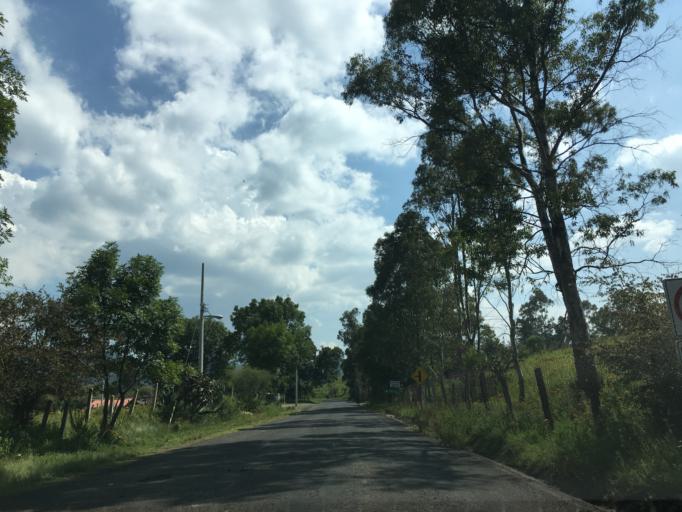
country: MX
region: Michoacan
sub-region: Morelia
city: Montana Monarca (Punta Altozano)
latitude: 19.6060
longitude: -101.1941
